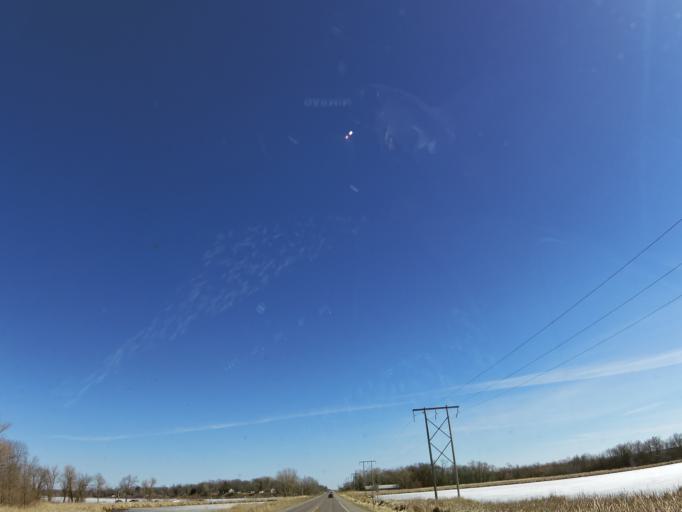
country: US
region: Minnesota
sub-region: Wright County
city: Maple Lake
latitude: 45.2269
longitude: -93.9826
